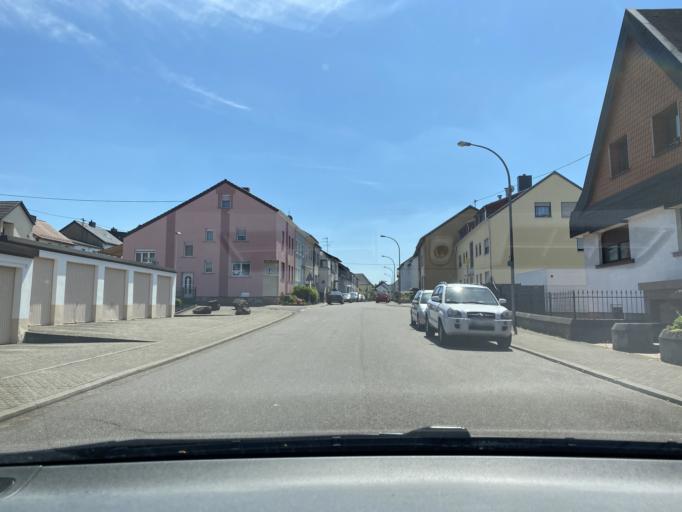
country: DE
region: Saarland
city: Saarlouis
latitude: 49.3271
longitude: 6.7726
